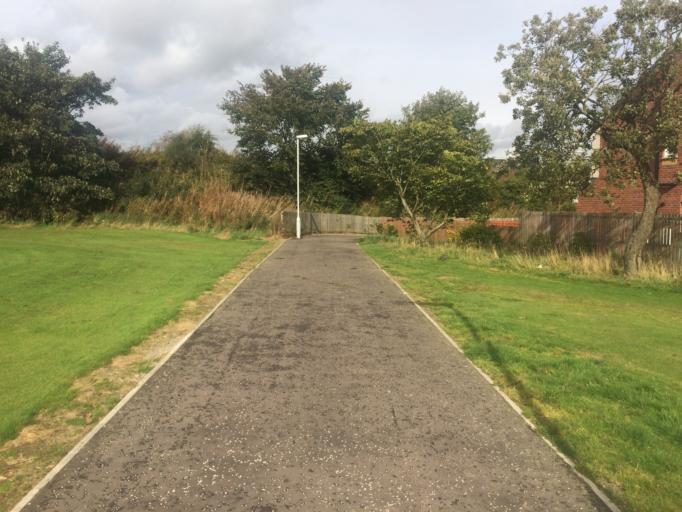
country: GB
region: Scotland
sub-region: Fife
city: Kelty
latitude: 56.1367
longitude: -3.3779
